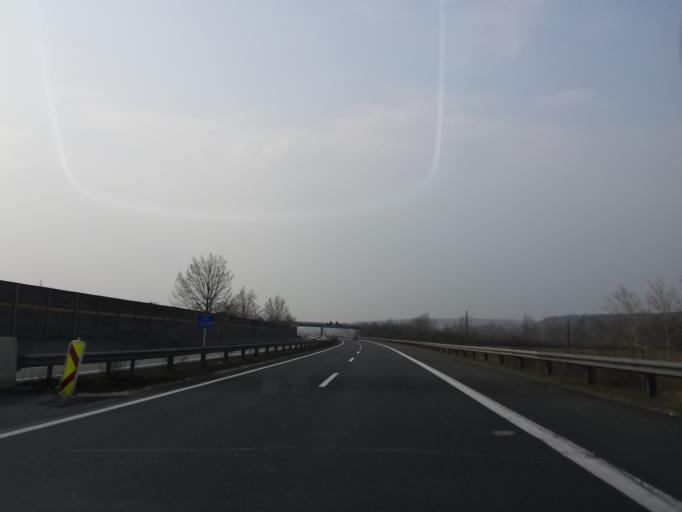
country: AT
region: Styria
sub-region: Politischer Bezirk Hartberg-Fuerstenfeld
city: Nestelbach im Ilztal
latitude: 47.0859
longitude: 15.8739
